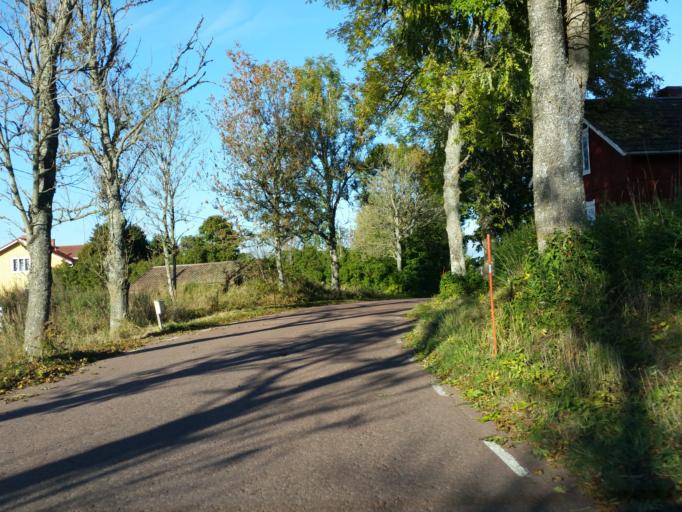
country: AX
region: Mariehamns stad
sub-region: Mariehamn
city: Mariehamn
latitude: 60.1258
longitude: 19.8277
